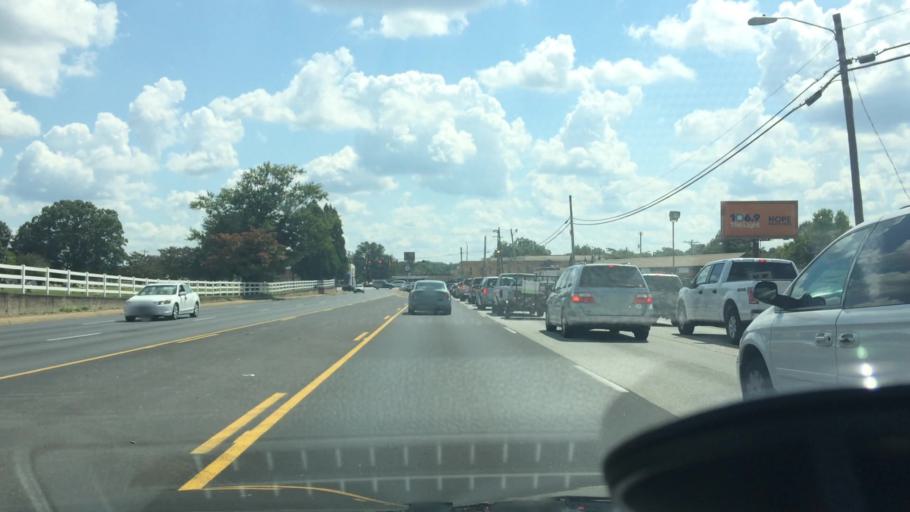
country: US
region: South Carolina
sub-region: Greenville County
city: Wade Hampton
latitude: 34.8796
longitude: -82.3634
